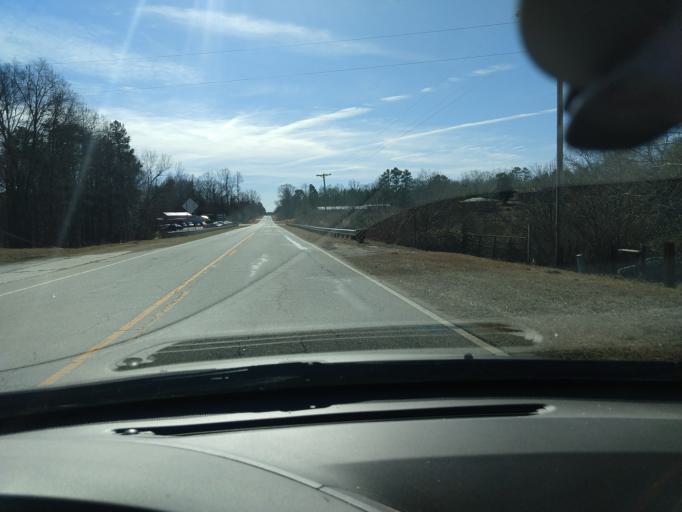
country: US
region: South Carolina
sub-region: Oconee County
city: Westminster
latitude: 34.6522
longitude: -83.1331
